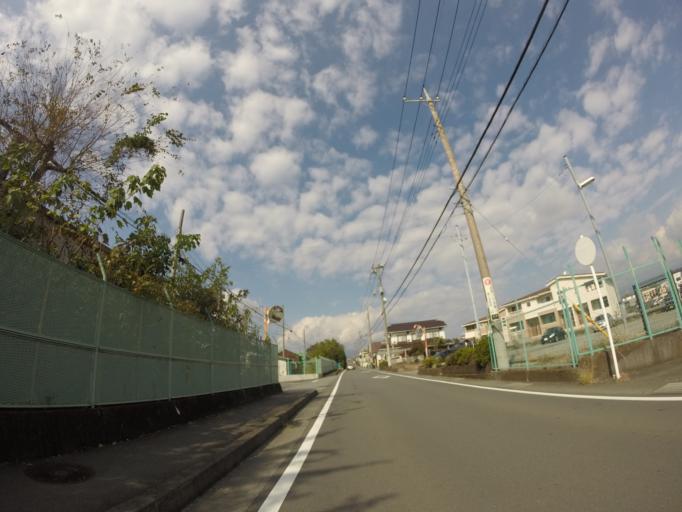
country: JP
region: Shizuoka
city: Fujinomiya
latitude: 35.2079
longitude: 138.6321
